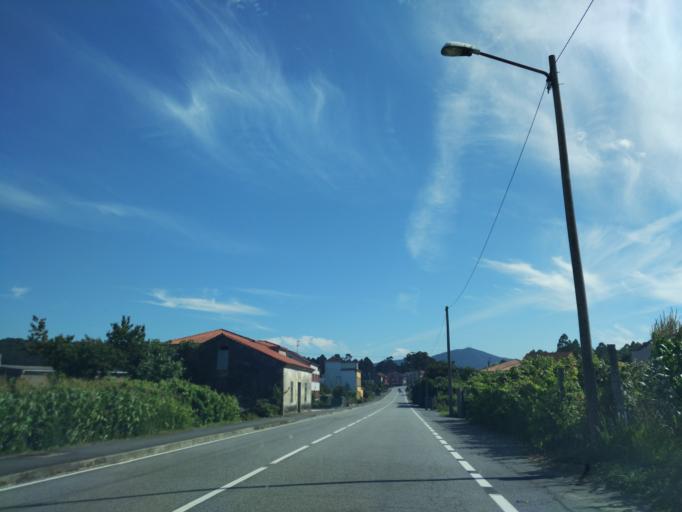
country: ES
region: Galicia
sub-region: Provincia da Coruna
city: Padron
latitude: 42.7181
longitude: -8.6861
